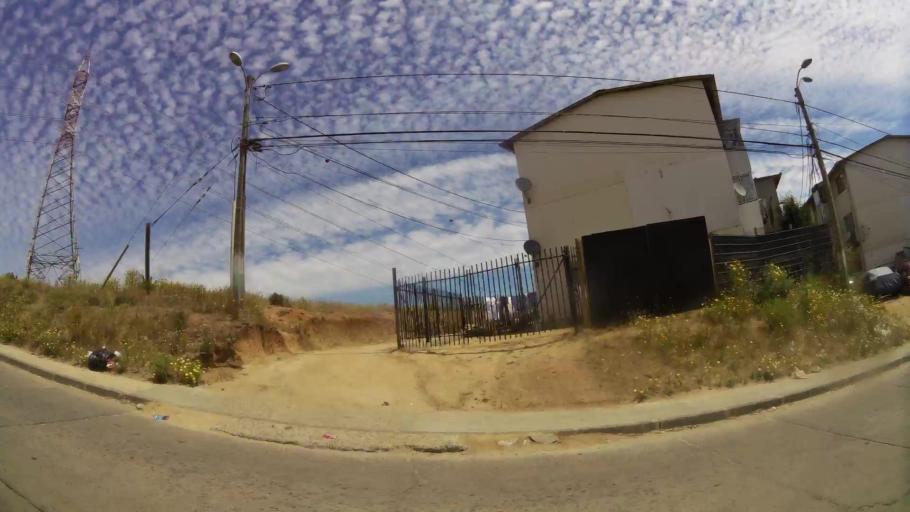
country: CL
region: Valparaiso
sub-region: Provincia de Valparaiso
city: Vina del Mar
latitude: -33.0582
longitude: -71.5632
